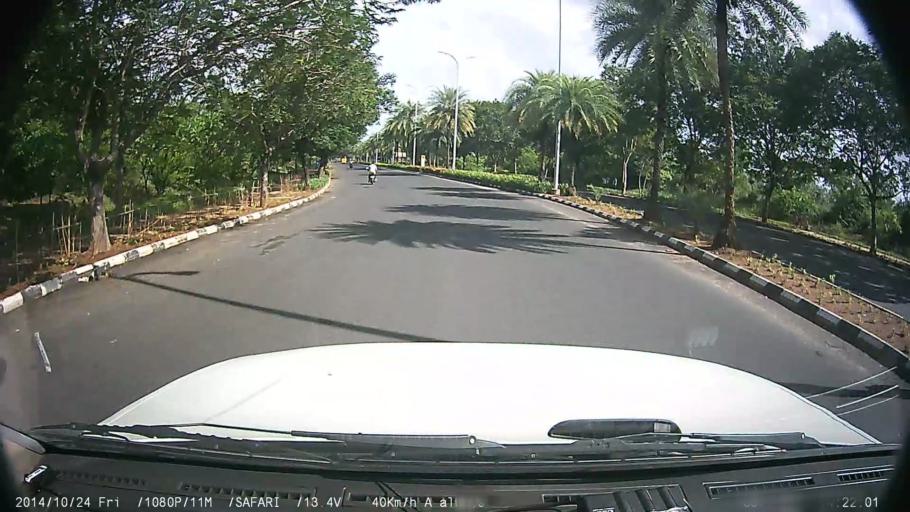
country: IN
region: Tamil Nadu
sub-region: Kancheepuram
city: Singapperumalkovil
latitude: 12.7416
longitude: 79.9929
